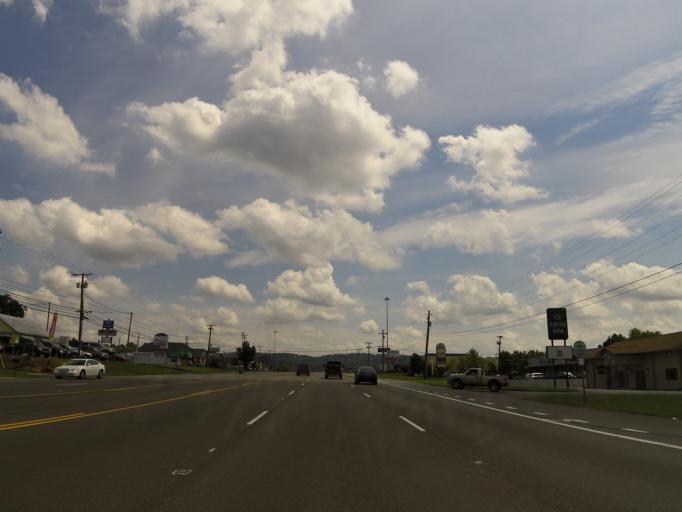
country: US
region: Tennessee
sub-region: Sullivan County
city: Kingsport
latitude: 36.5499
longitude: -82.5242
